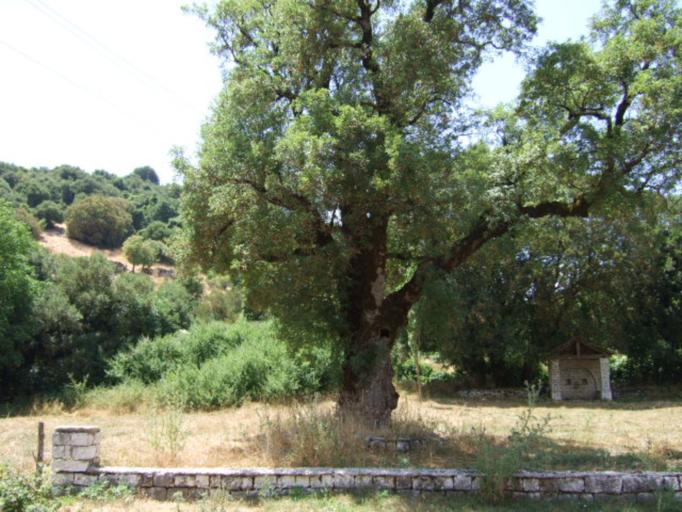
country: GR
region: Epirus
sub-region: Nomos Ioanninon
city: Kalpaki
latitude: 39.8794
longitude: 20.6787
